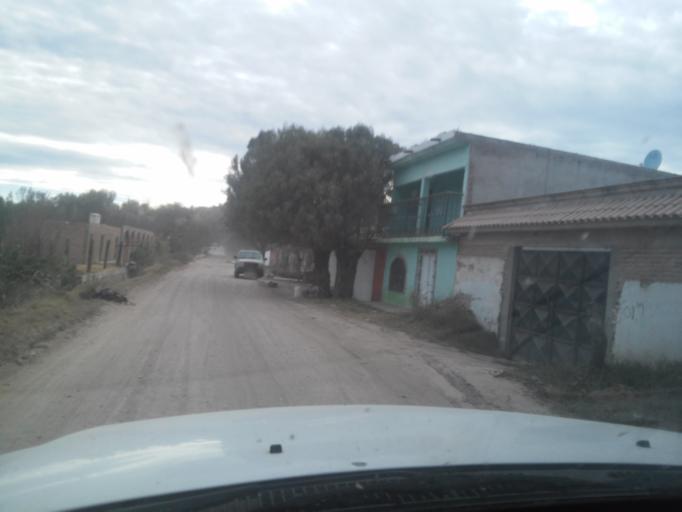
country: MX
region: Durango
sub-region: Durango
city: Jose Refugio Salcido
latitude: 24.0477
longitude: -104.5489
